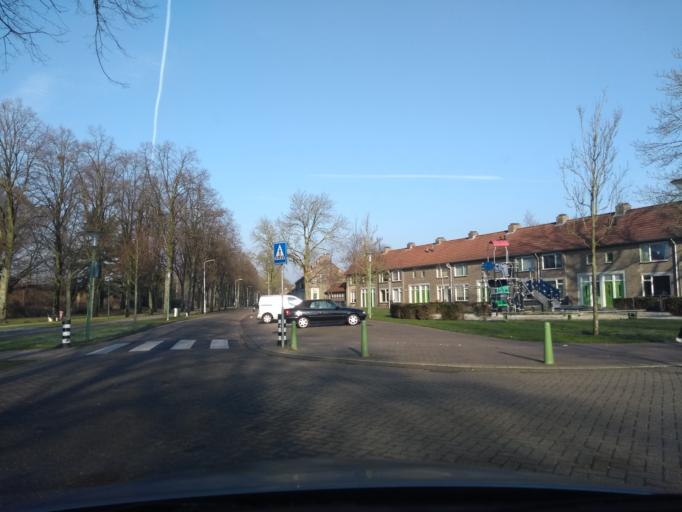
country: NL
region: North Brabant
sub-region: Gemeente Eindhoven
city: Eindhoven
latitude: 51.4530
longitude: 5.4548
